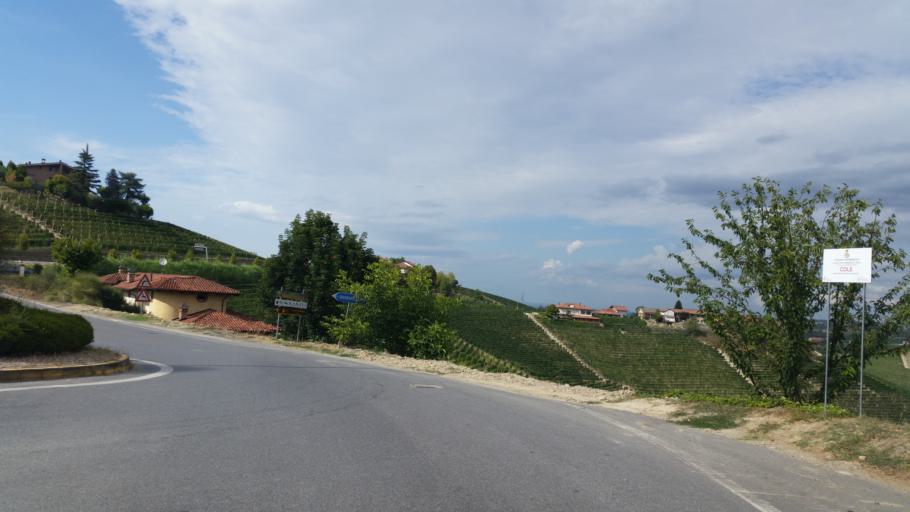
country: IT
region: Piedmont
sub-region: Provincia di Cuneo
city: Barbaresco
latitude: 44.7219
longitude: 8.0840
